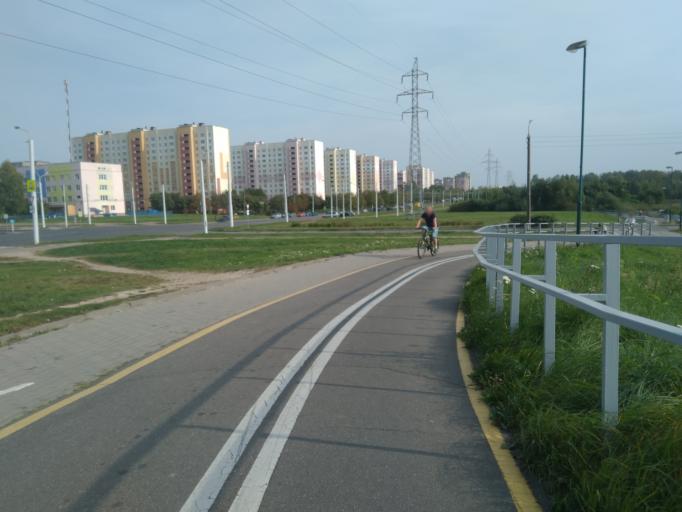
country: BY
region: Minsk
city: Minsk
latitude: 53.8587
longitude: 27.5896
